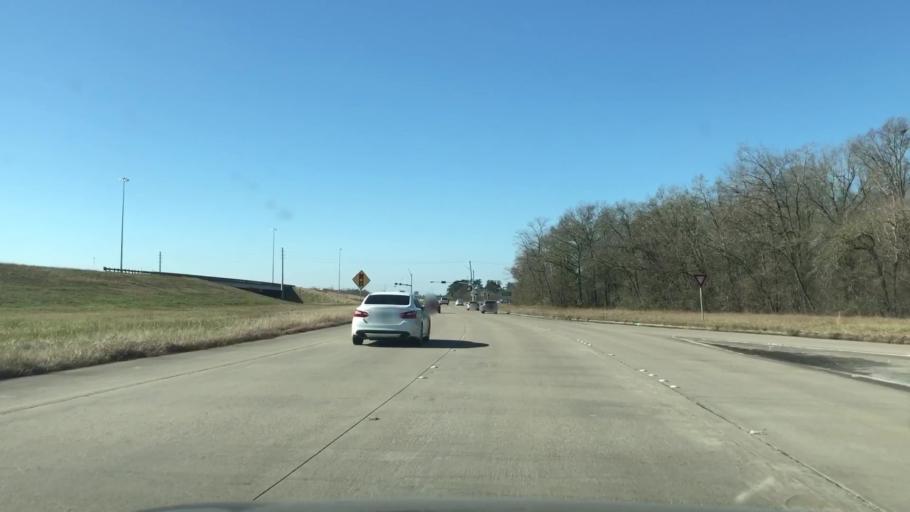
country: US
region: Texas
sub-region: Harris County
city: Cloverleaf
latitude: 29.8316
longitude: -95.1803
